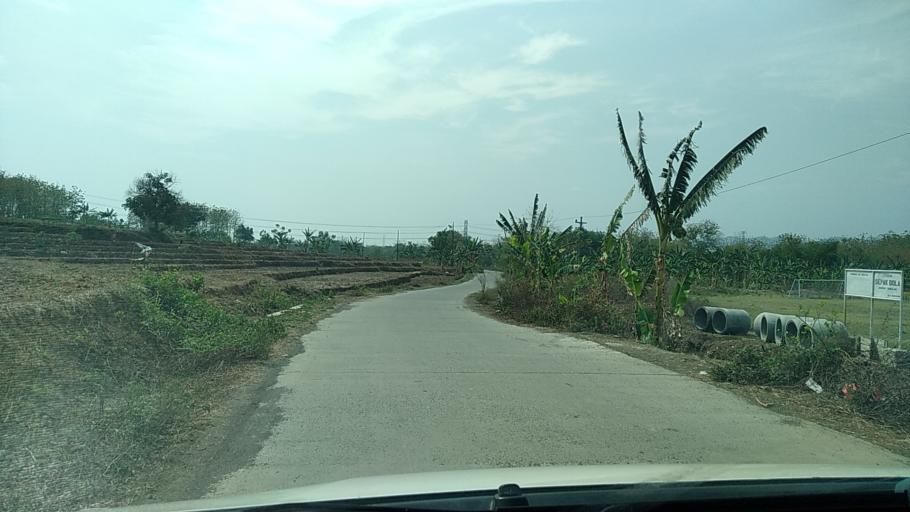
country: ID
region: Central Java
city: Mranggen
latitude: -7.0643
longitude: 110.4886
